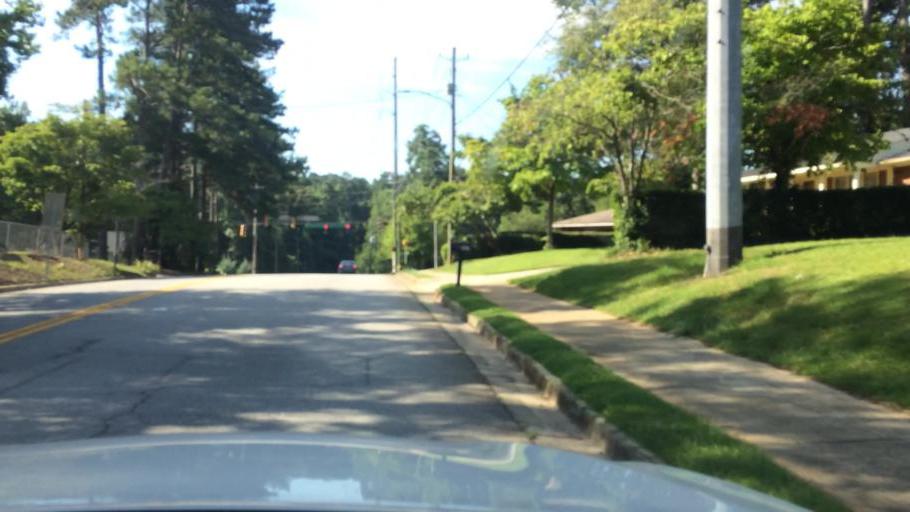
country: US
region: Georgia
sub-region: Columbia County
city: Martinez
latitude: 33.4953
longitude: -82.0385
